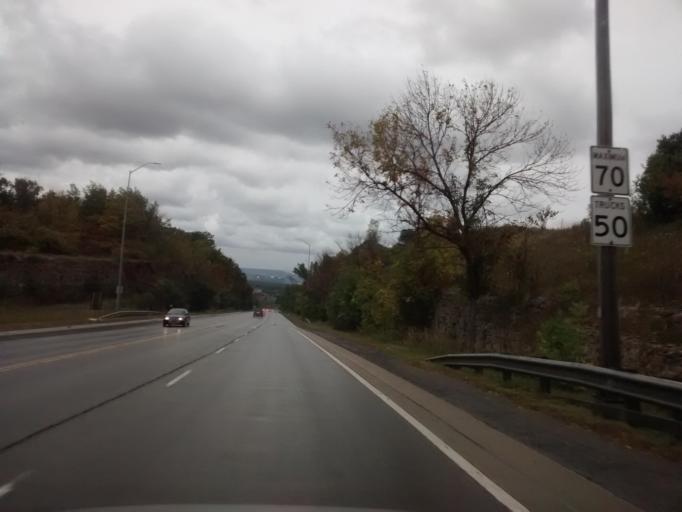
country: CA
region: Ontario
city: Hamilton
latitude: 43.2055
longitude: -79.7645
